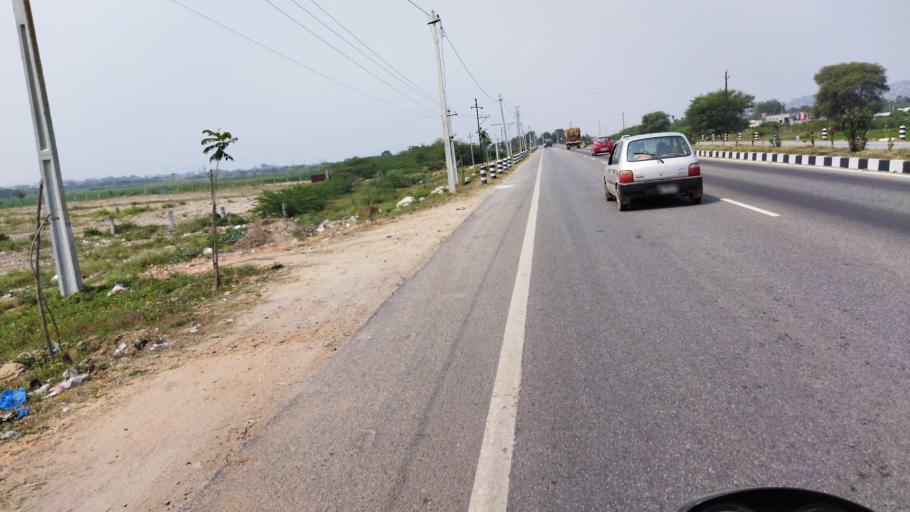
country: IN
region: Telangana
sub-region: Nalgonda
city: Nalgonda
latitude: 17.0772
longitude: 79.2812
